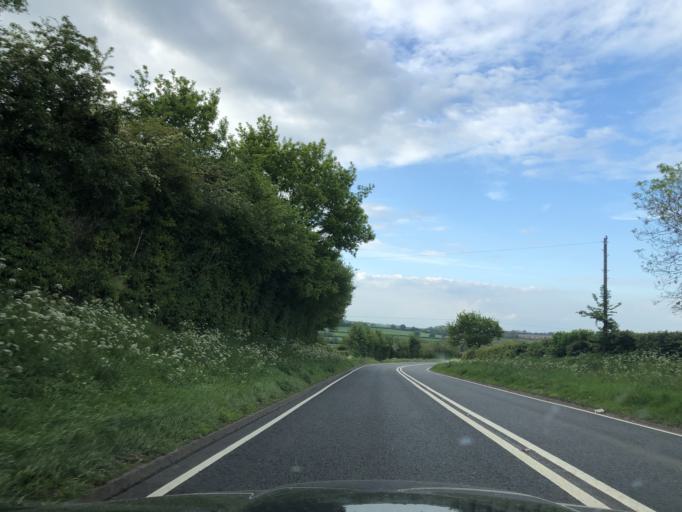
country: GB
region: England
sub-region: Gloucestershire
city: Moreton in Marsh
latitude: 52.0151
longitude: -1.6903
